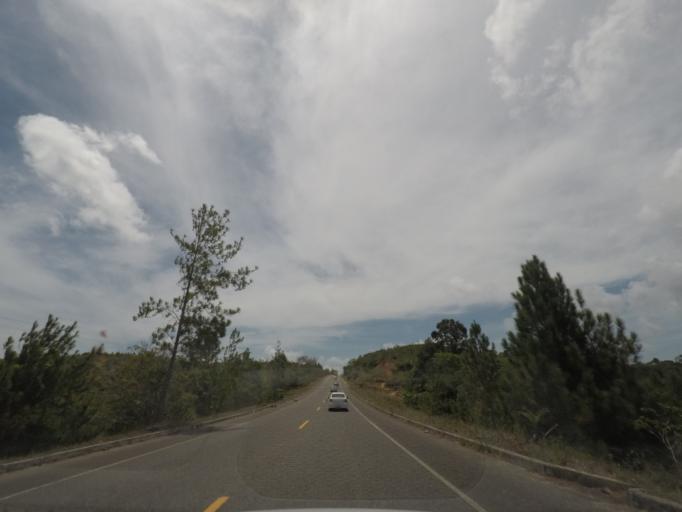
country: BR
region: Bahia
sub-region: Conde
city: Conde
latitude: -11.9224
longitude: -37.6660
